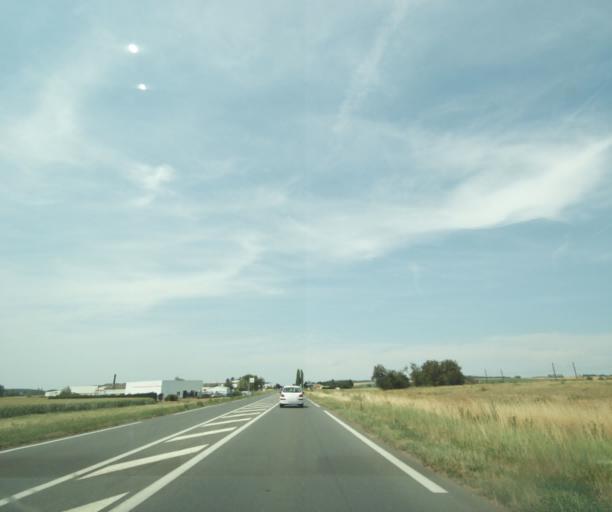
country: FR
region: Poitou-Charentes
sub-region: Departement de la Vienne
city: Dange-Saint-Romain
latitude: 46.9441
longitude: 0.6073
